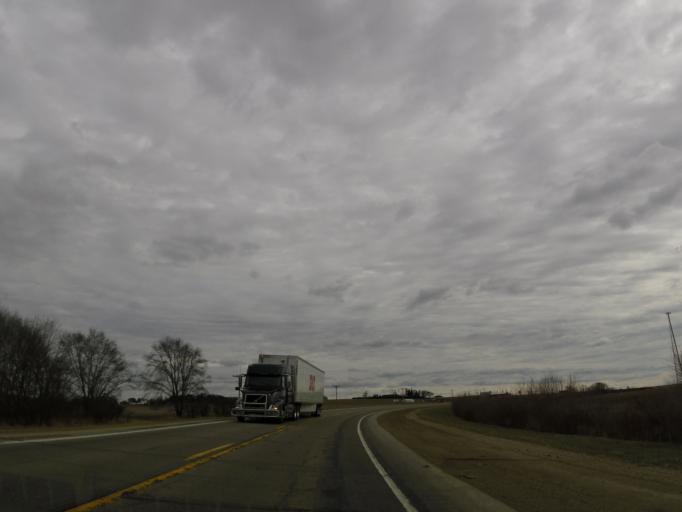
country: US
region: Iowa
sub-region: Howard County
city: Cresco
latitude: 43.4562
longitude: -92.2993
